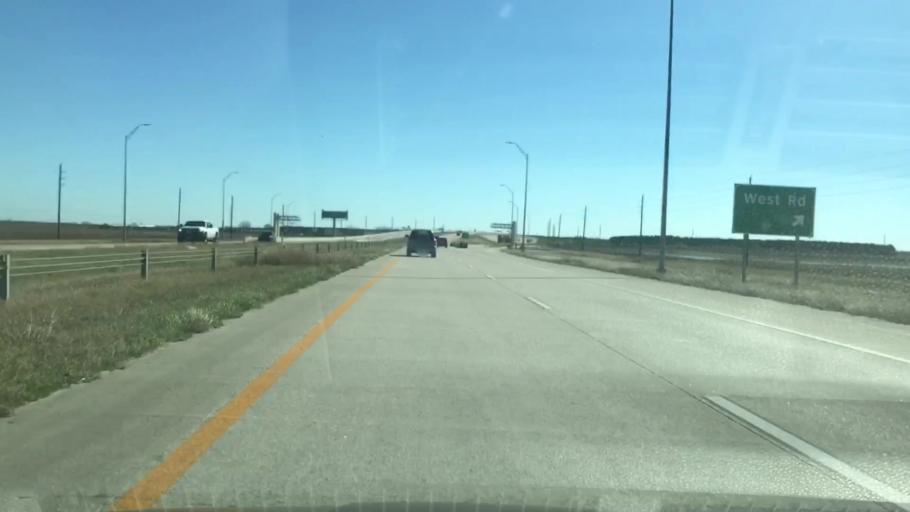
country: US
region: Texas
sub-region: Harris County
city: Cypress
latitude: 29.9098
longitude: -95.7608
